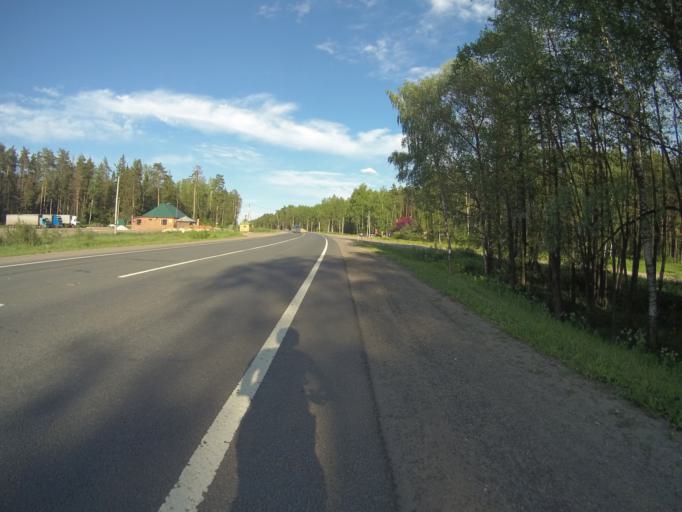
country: RU
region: Vladimir
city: Kameshkovo
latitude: 56.1935
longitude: 40.9270
